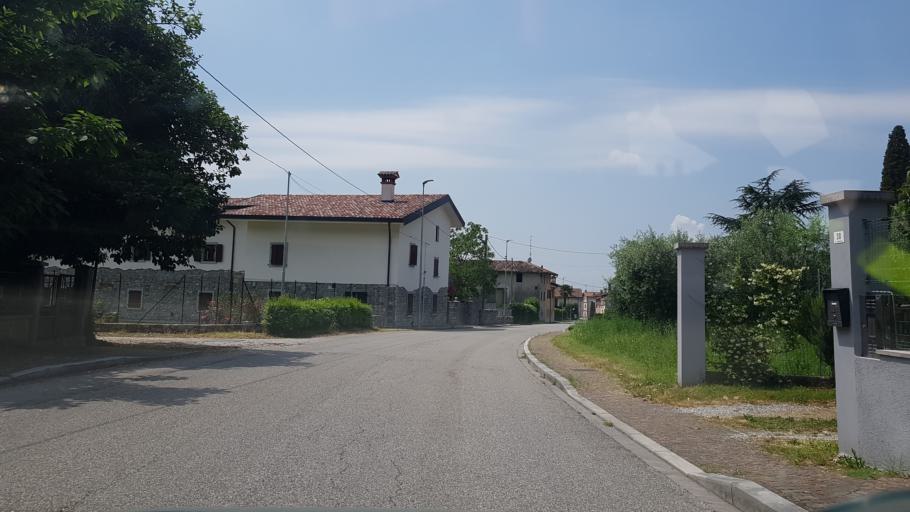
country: IT
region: Friuli Venezia Giulia
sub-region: Provincia di Udine
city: Torreano
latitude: 46.1289
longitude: 13.4320
